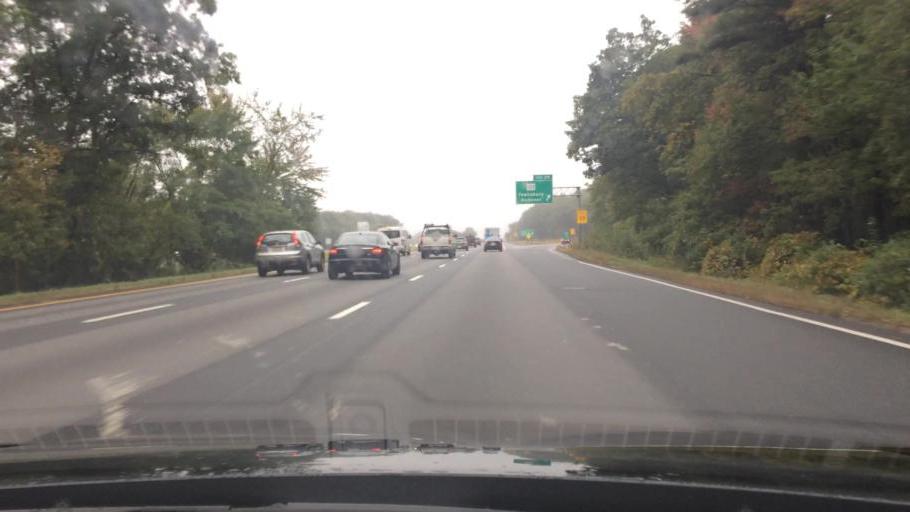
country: US
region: Massachusetts
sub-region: Middlesex County
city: Tewksbury
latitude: 42.6457
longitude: -71.2264
